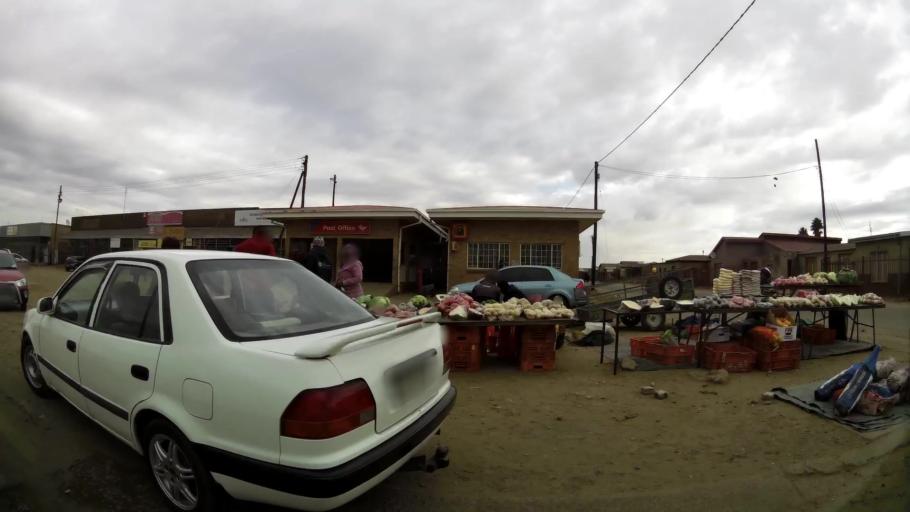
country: ZA
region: Orange Free State
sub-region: Fezile Dabi District Municipality
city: Kroonstad
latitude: -27.6500
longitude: 27.1974
